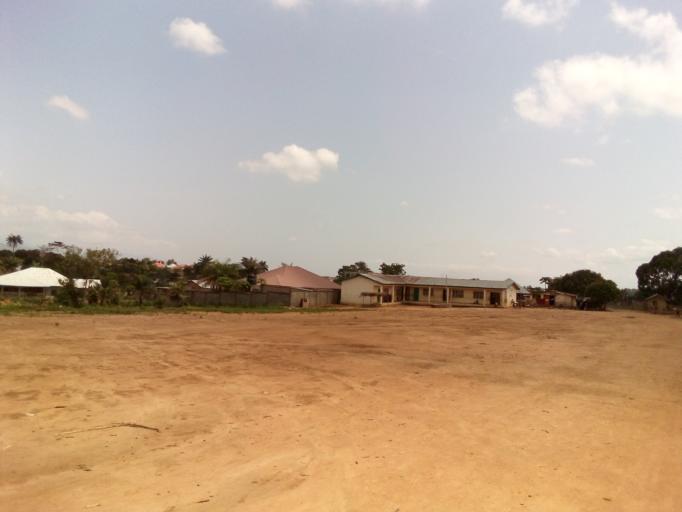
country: SL
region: Western Area
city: Waterloo
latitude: 8.3365
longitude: -13.0195
